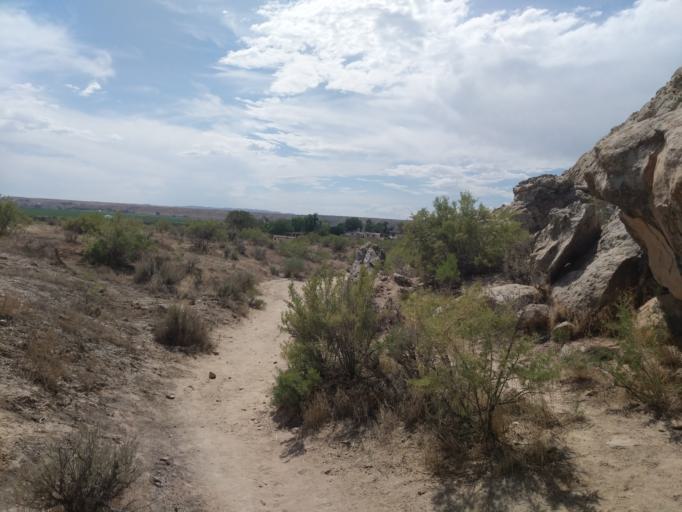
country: US
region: Utah
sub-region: Uintah County
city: Naples
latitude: 40.4377
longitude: -109.2986
